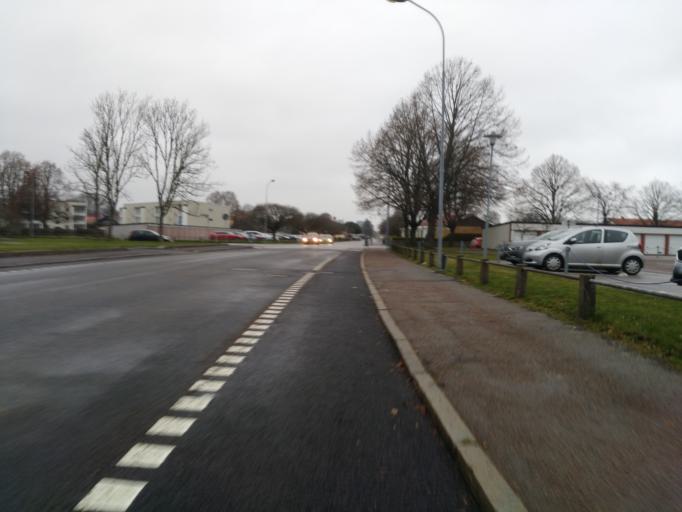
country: SE
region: Vaestra Goetaland
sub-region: Lidkopings Kommun
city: Lidkoping
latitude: 58.4935
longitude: 13.1568
